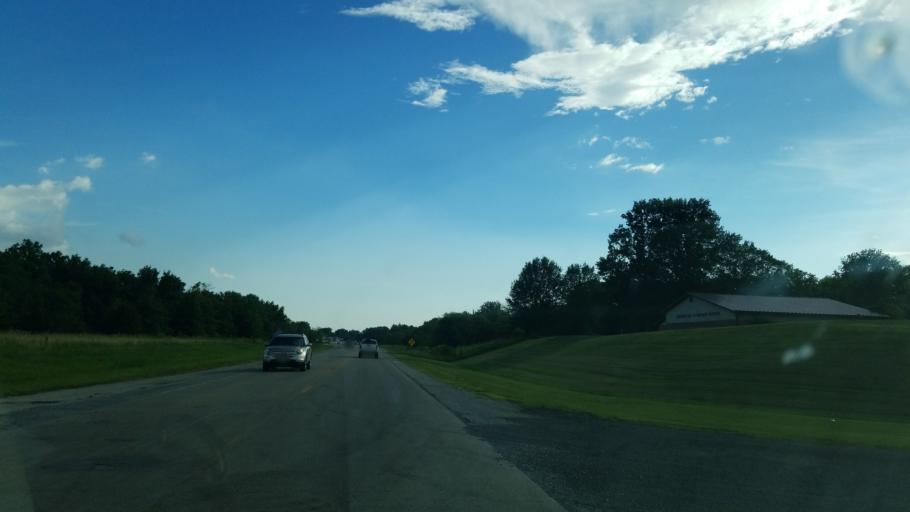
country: US
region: Illinois
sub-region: Marion County
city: Central City
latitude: 38.5607
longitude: -89.1220
